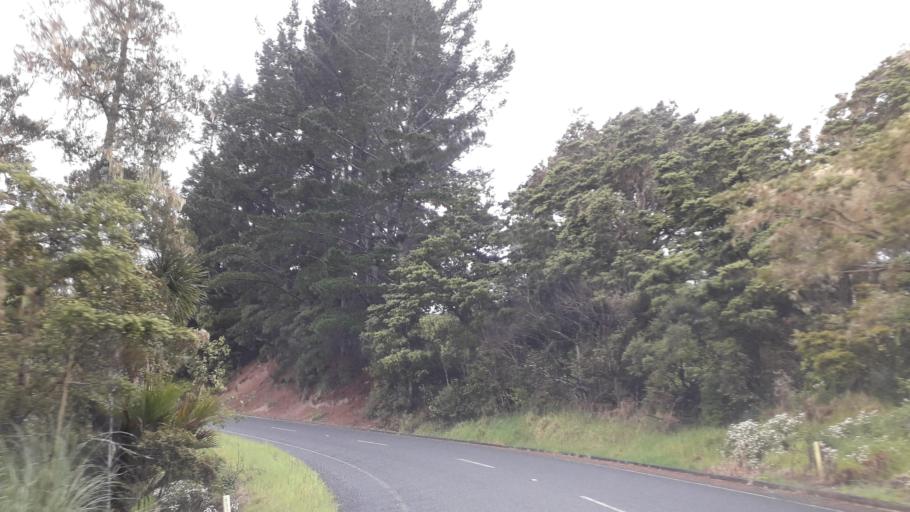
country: NZ
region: Northland
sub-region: Far North District
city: Kaitaia
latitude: -35.3583
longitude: 173.4866
